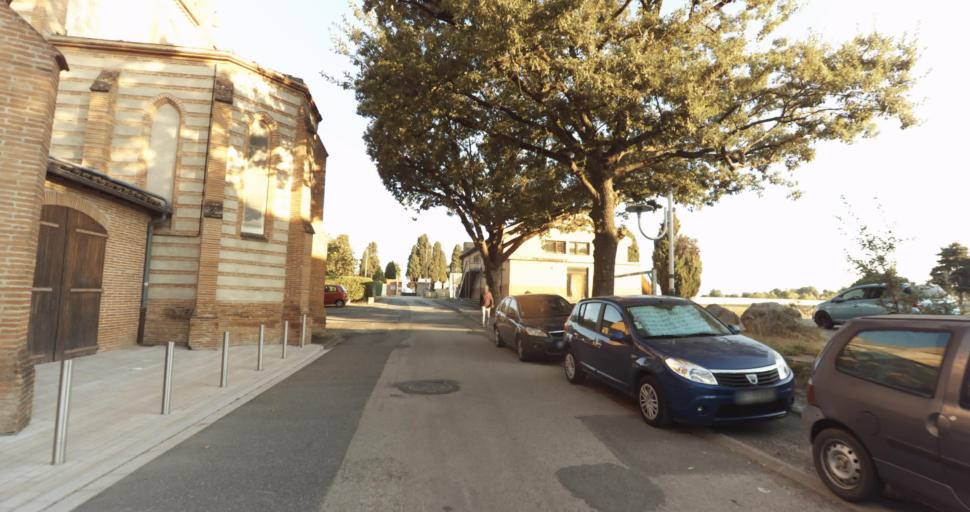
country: FR
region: Midi-Pyrenees
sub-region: Departement de la Haute-Garonne
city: L'Union
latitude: 43.6588
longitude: 1.4838
